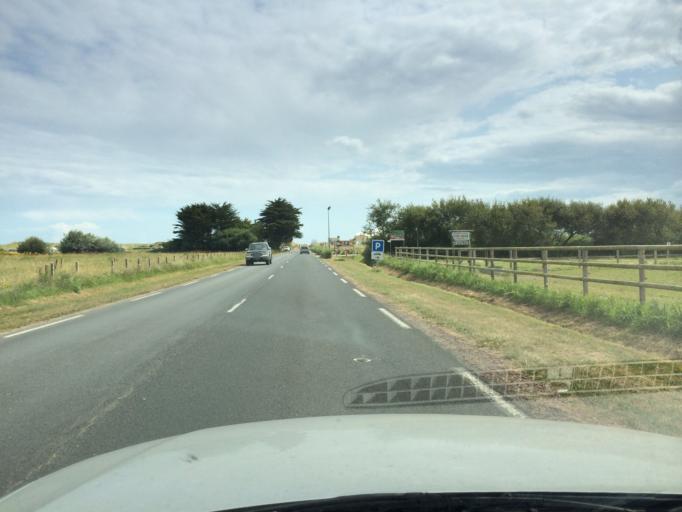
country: FR
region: Lower Normandy
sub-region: Departement de la Manche
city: Saint-Hilaire-Petitville
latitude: 49.4139
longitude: -1.1802
